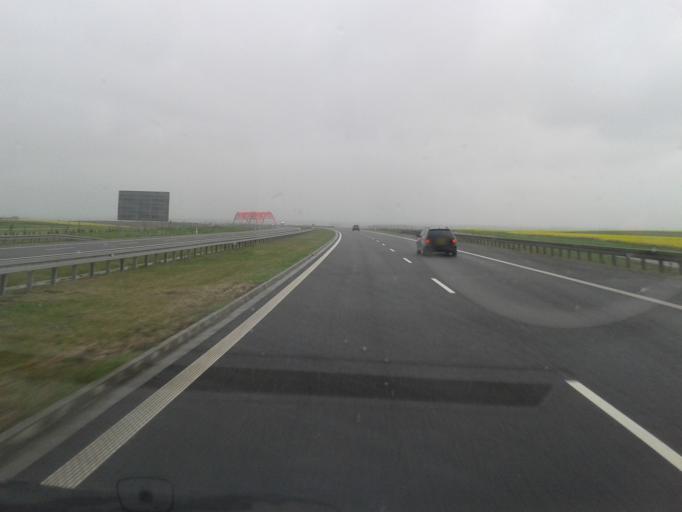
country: PL
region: Subcarpathian Voivodeship
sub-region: Powiat przeworski
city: Mirocin
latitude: 50.0555
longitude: 22.5699
